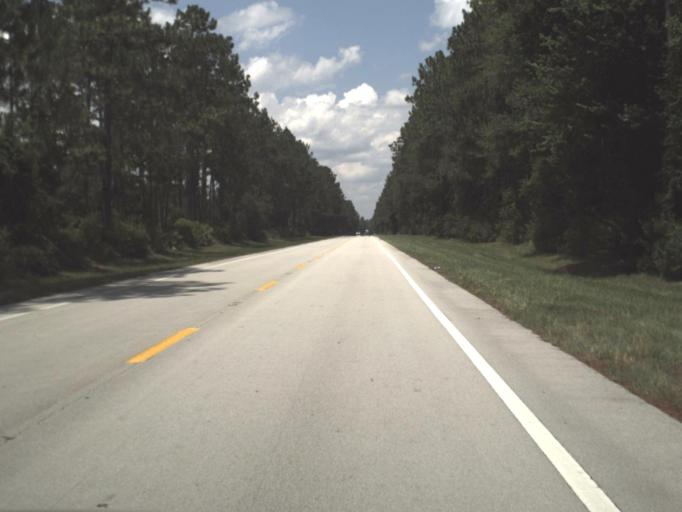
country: US
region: Florida
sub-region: Baker County
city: Macclenny
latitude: 30.1551
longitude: -82.1851
